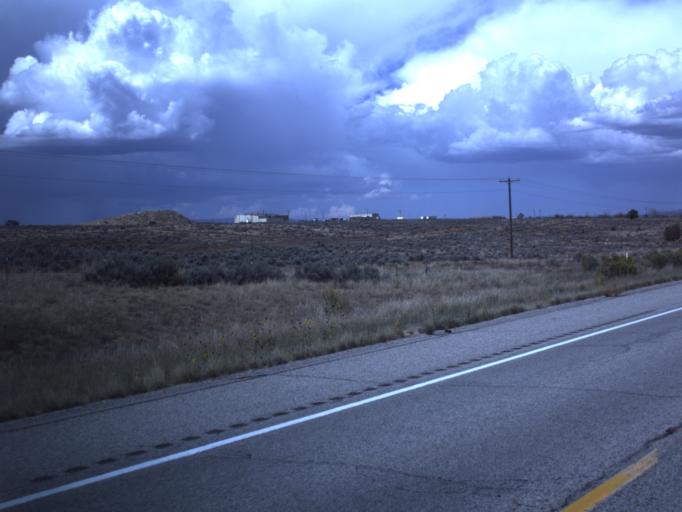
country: US
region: Utah
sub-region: San Juan County
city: Blanding
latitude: 37.5284
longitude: -109.4941
